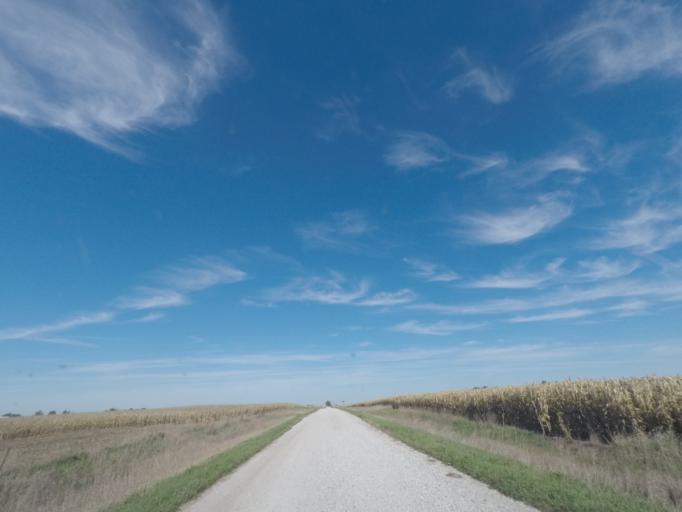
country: US
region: Iowa
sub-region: Story County
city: Nevada
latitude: 42.0149
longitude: -93.3573
